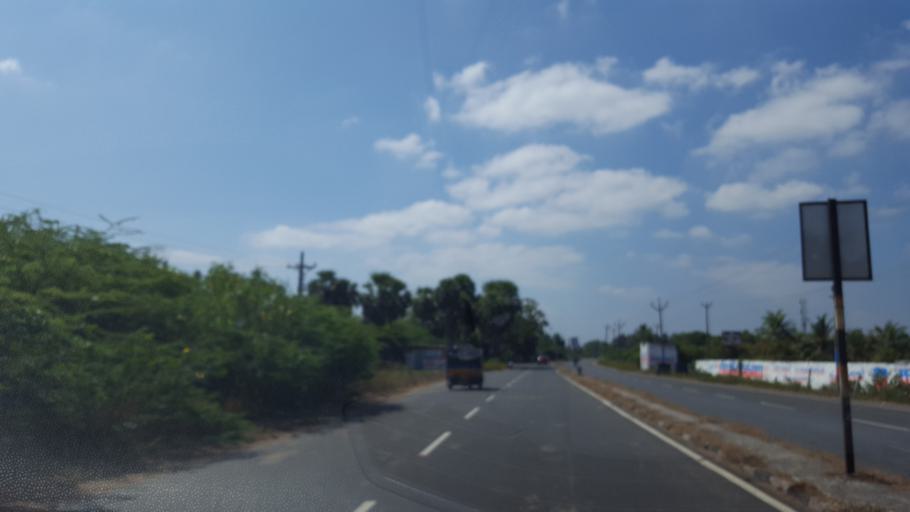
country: IN
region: Tamil Nadu
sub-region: Kancheepuram
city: Mamallapuram
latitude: 12.6432
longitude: 80.1741
